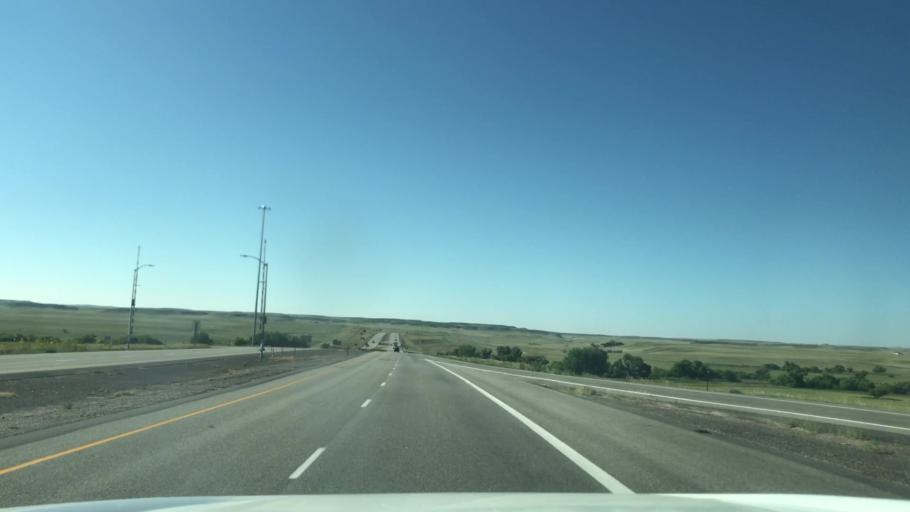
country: US
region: Wyoming
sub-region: Platte County
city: Wheatland
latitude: 41.7545
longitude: -104.8324
